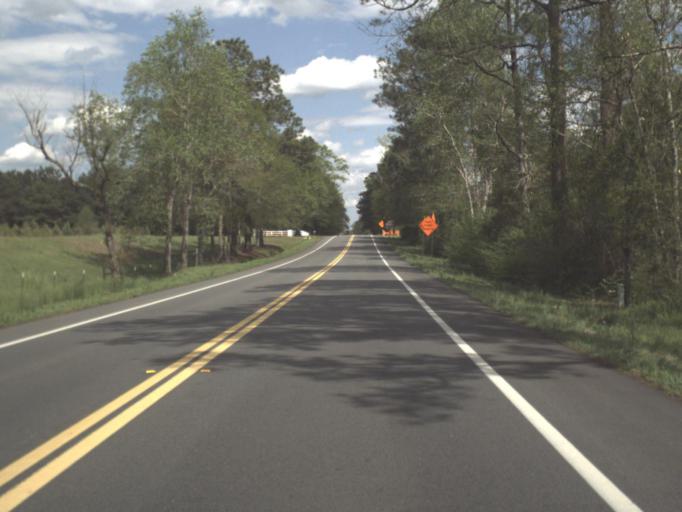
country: US
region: Alabama
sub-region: Covington County
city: Florala
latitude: 30.9666
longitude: -86.3944
